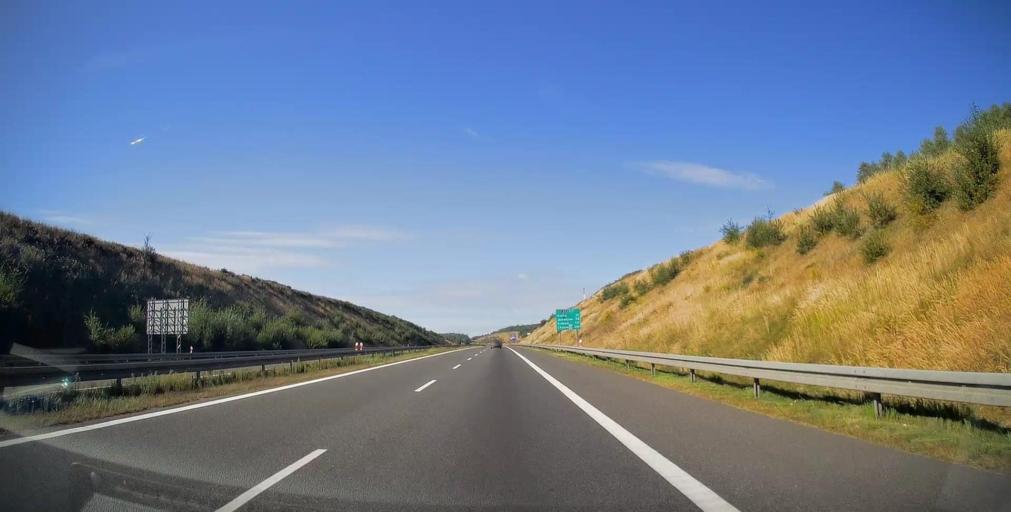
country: PL
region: Swietokrzyskie
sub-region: Powiat skarzyski
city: Laczna
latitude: 50.9890
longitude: 20.7673
